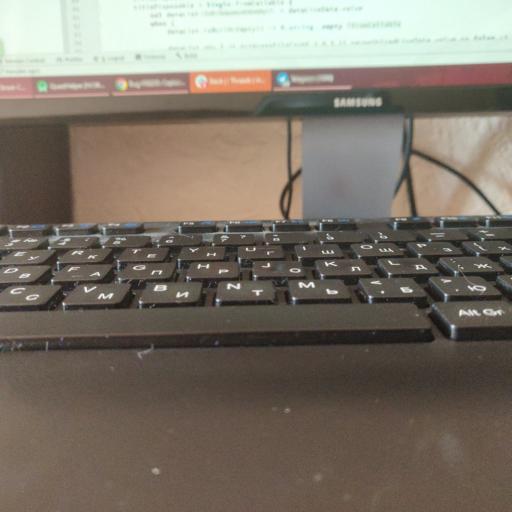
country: FI
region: Haeme
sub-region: Forssa
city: Jokioinen
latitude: 60.8468
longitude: 23.4180
